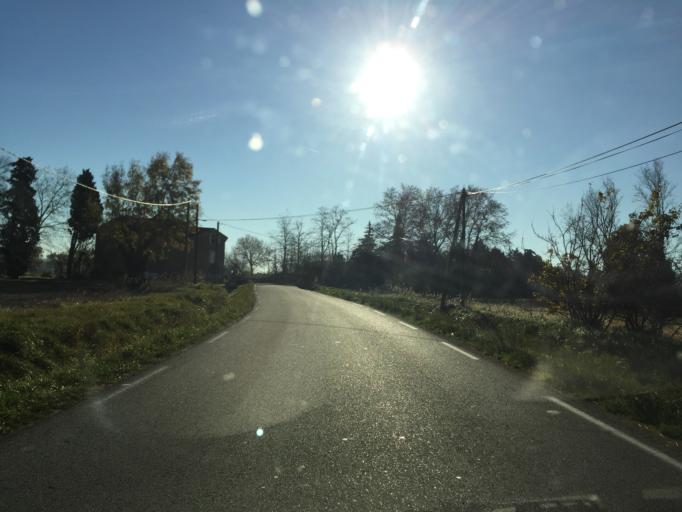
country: FR
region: Provence-Alpes-Cote d'Azur
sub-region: Departement du Vaucluse
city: Bedarrides
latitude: 44.0343
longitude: 4.9112
